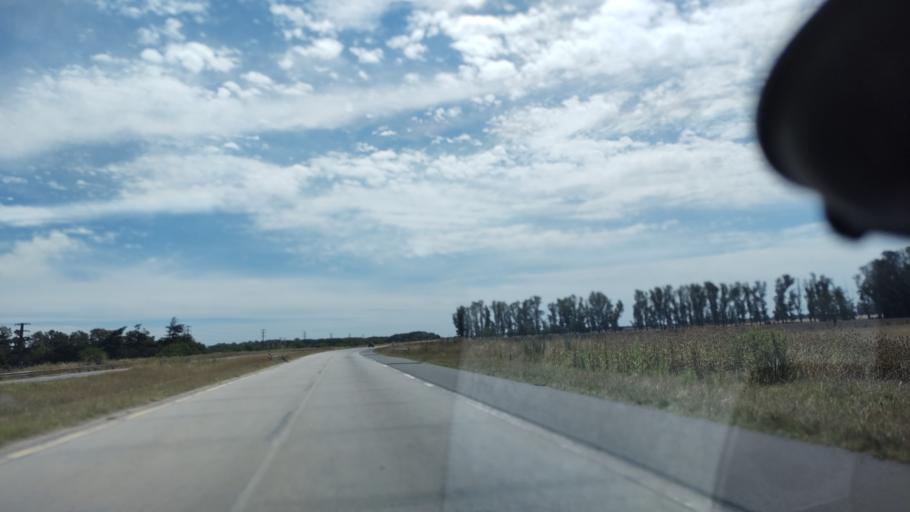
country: AR
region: Buenos Aires
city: Canuelas
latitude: -35.0781
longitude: -58.6706
